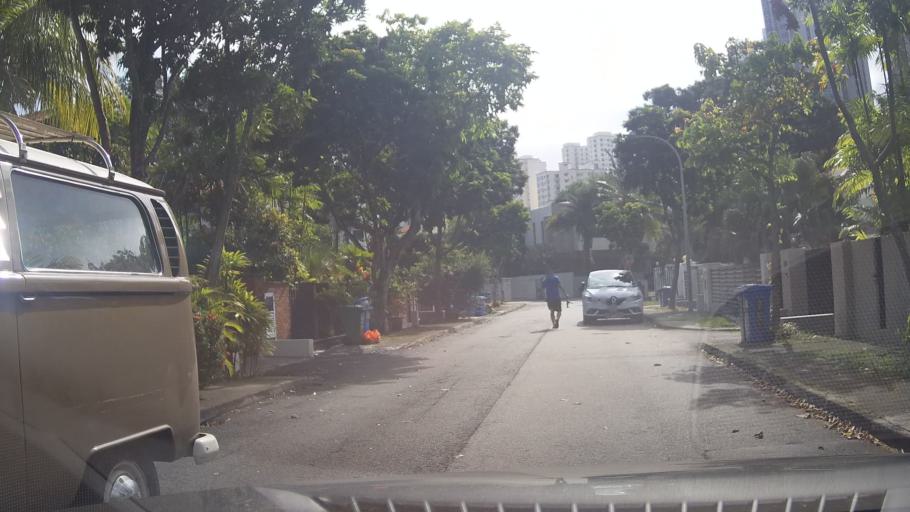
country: SG
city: Singapore
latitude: 1.2984
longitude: 103.8905
